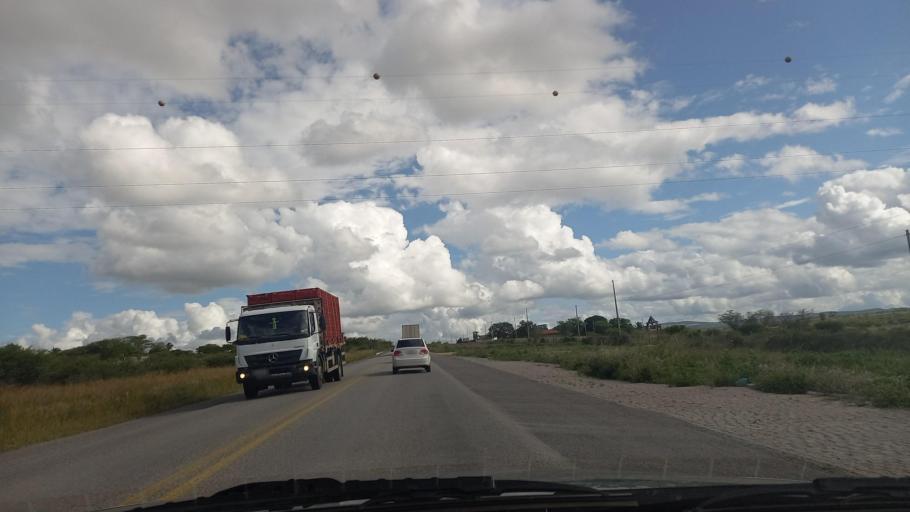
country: BR
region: Pernambuco
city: Garanhuns
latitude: -8.8069
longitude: -36.4421
